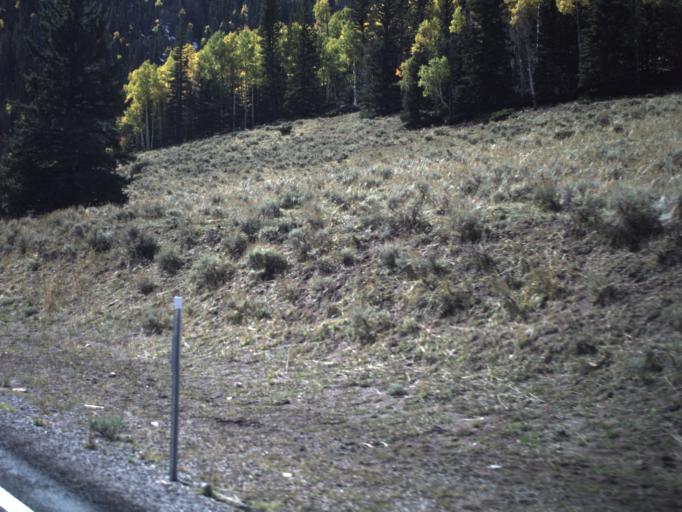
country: US
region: Utah
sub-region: Beaver County
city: Beaver
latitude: 38.2911
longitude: -112.4434
